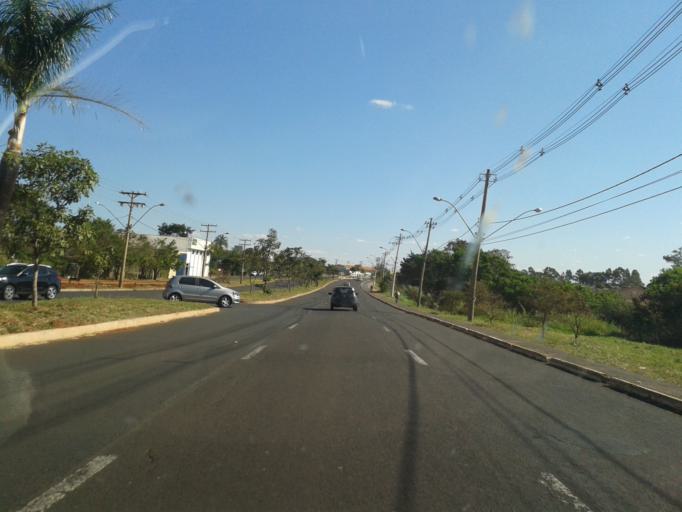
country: BR
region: Minas Gerais
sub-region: Uberaba
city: Uberaba
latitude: -19.7475
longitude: -47.9689
